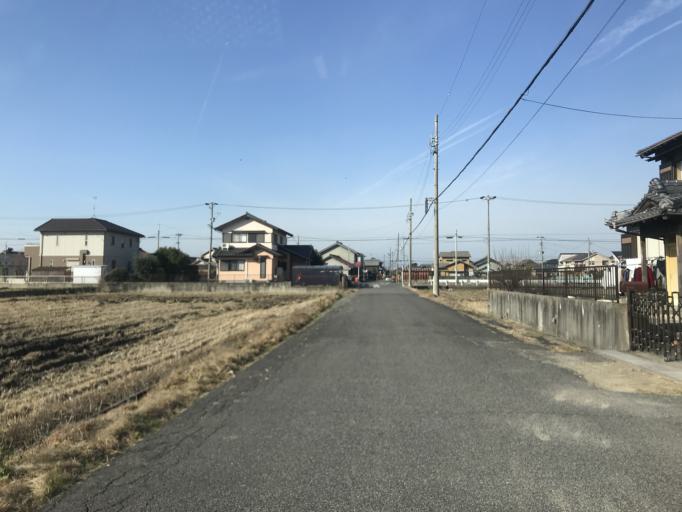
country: JP
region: Aichi
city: Iwakura
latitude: 35.2287
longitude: 136.8508
